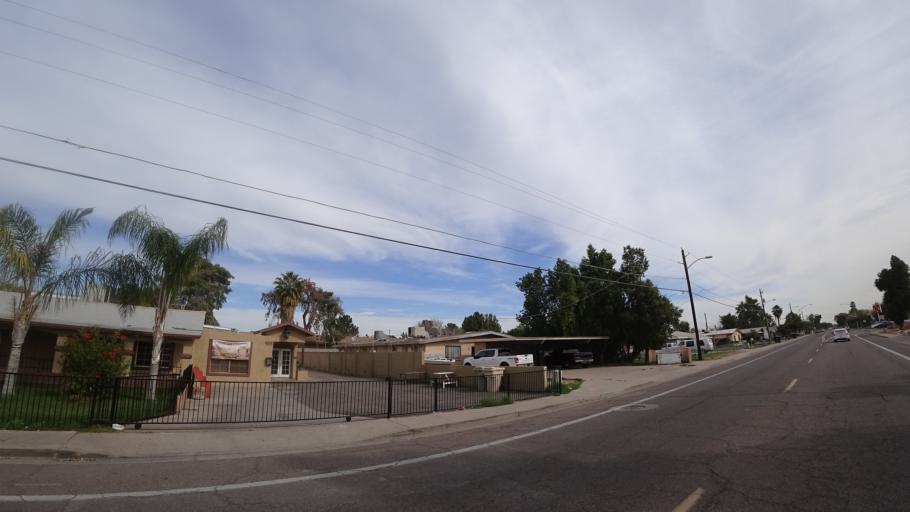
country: US
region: Arizona
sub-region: Maricopa County
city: Glendale
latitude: 33.5312
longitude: -112.1971
